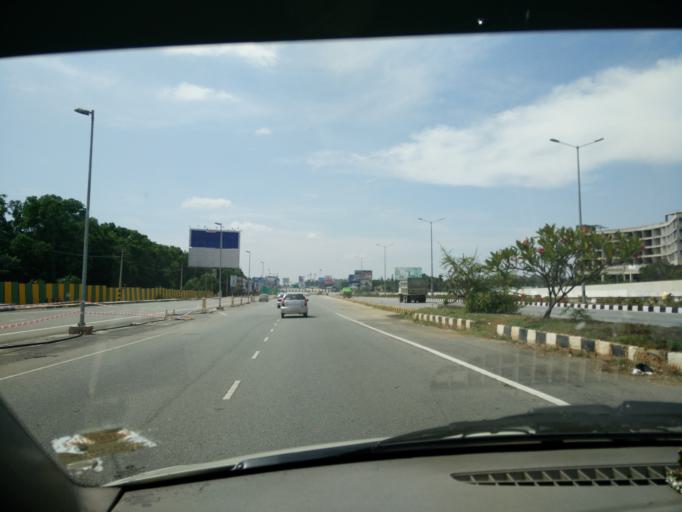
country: IN
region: Karnataka
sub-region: Bangalore Rural
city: Devanhalli
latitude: 13.1980
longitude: 77.6569
